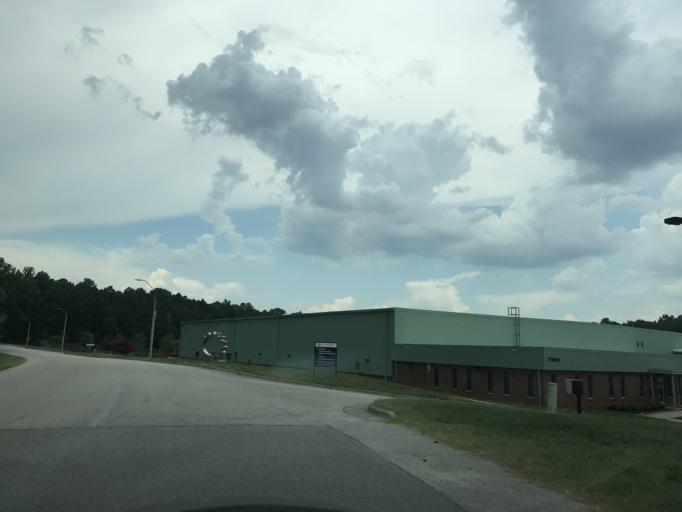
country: US
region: North Carolina
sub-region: Wake County
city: Wake Forest
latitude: 35.8871
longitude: -78.5769
